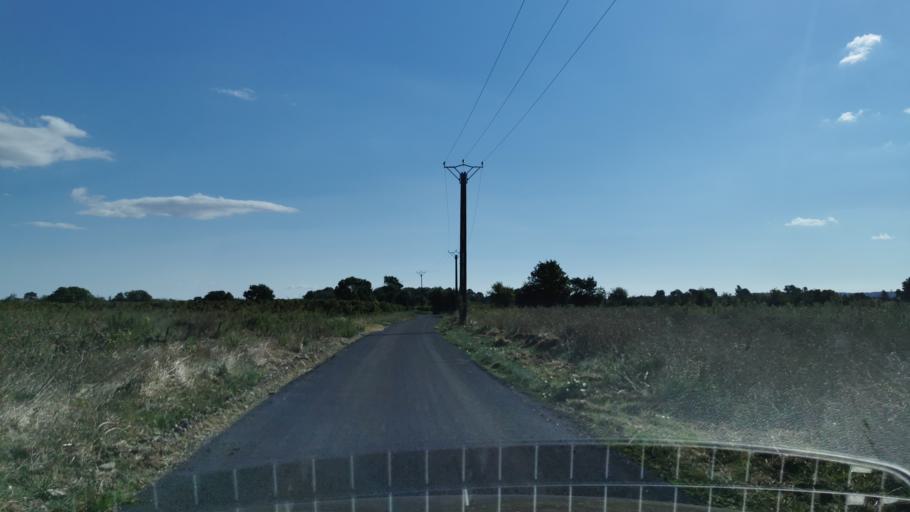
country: FR
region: Languedoc-Roussillon
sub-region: Departement de l'Aude
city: Ginestas
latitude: 43.2419
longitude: 2.8739
